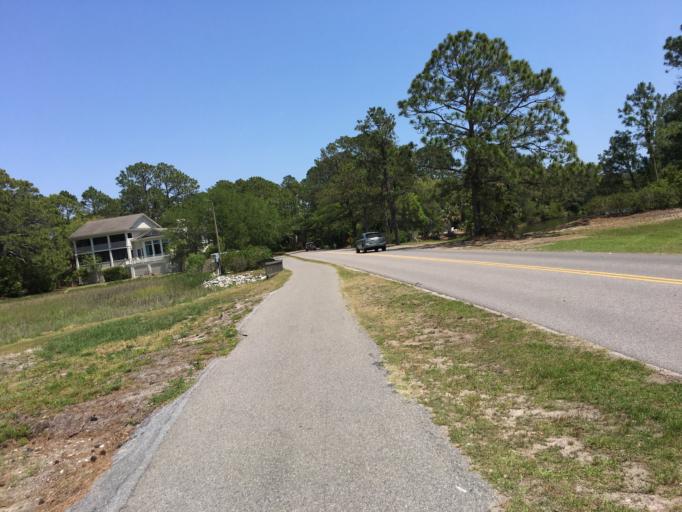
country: US
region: Georgia
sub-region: Chatham County
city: Tybee Island
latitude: 32.1123
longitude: -80.8168
